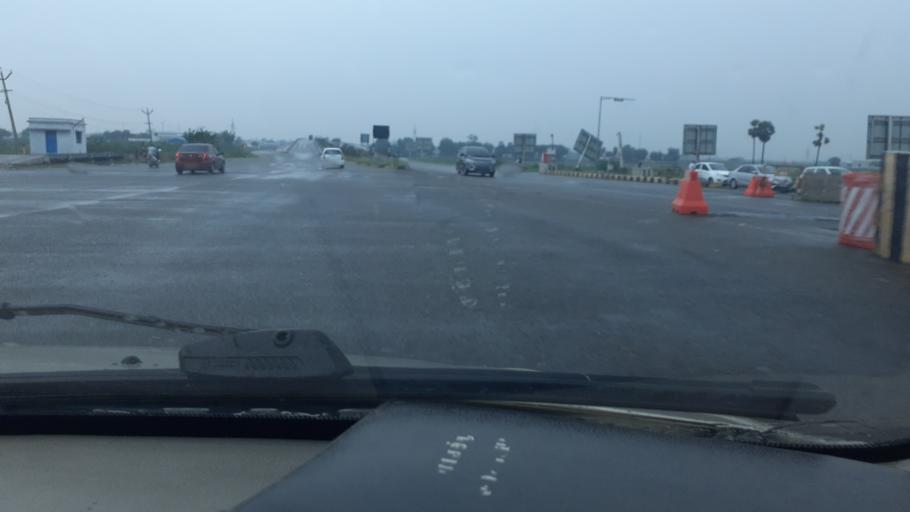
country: IN
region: Tamil Nadu
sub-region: Virudhunagar
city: Sattur
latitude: 9.3851
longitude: 77.9143
